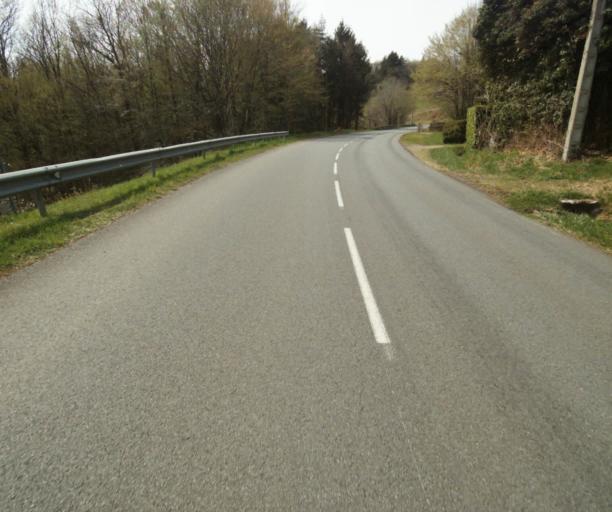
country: FR
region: Limousin
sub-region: Departement de la Correze
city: Naves
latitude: 45.3344
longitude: 1.7757
